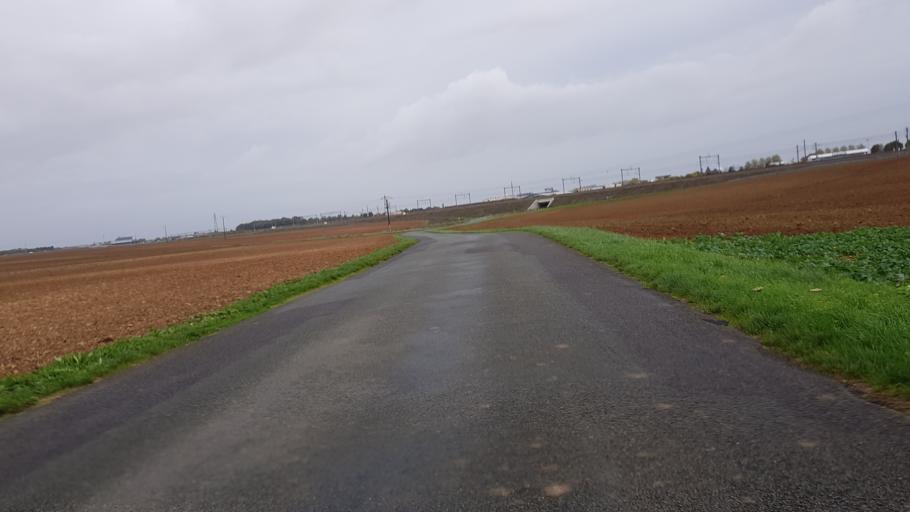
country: FR
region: Poitou-Charentes
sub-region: Departement de la Vienne
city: Chasseneuil-du-Poitou
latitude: 46.6630
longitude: 0.3502
